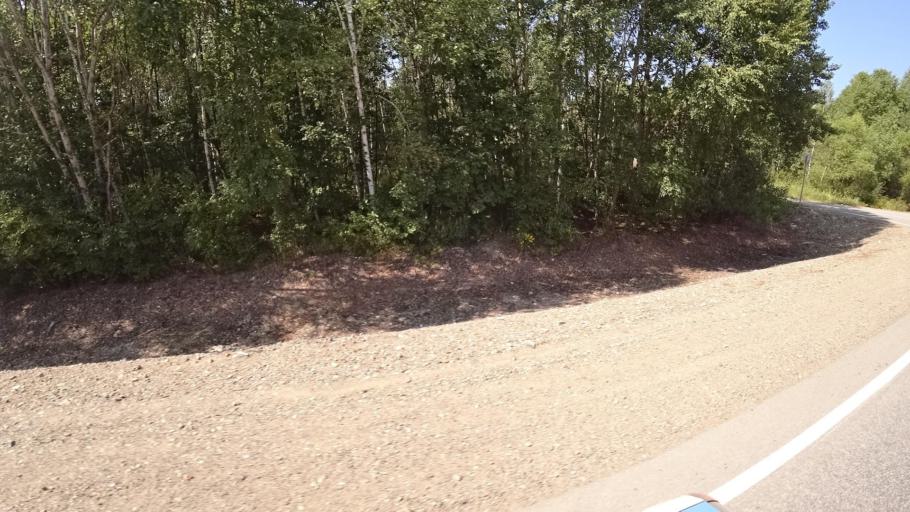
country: RU
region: Khabarovsk Krai
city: Khor
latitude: 47.9838
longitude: 135.0883
